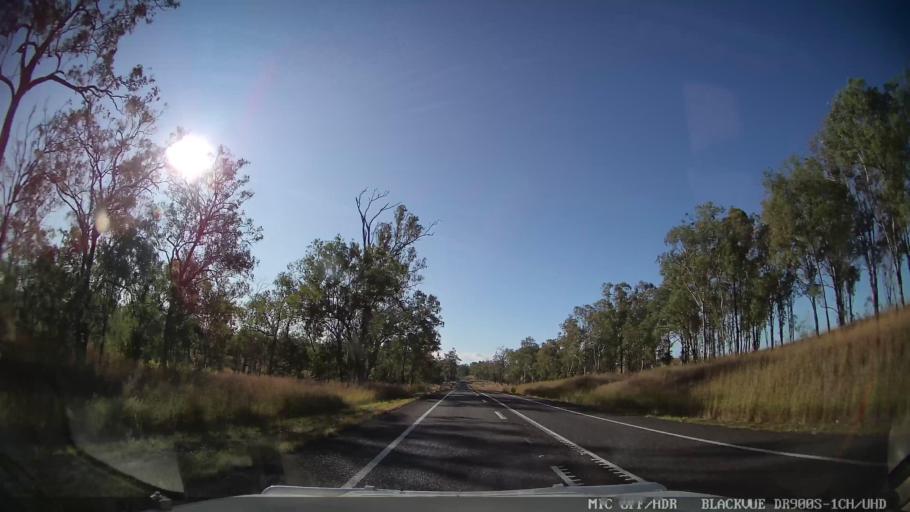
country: AU
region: Queensland
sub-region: Bundaberg
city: Sharon
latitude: -24.8362
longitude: 151.7100
